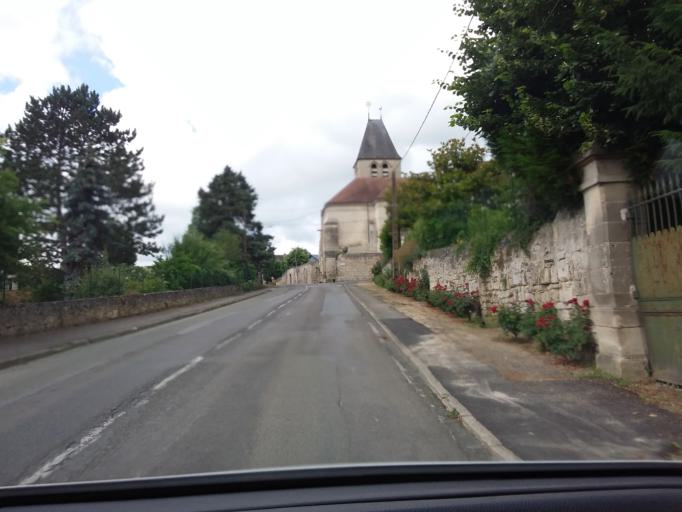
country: FR
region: Picardie
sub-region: Departement de l'Aisne
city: Vailly-sur-Aisne
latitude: 49.3980
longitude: 3.4712
